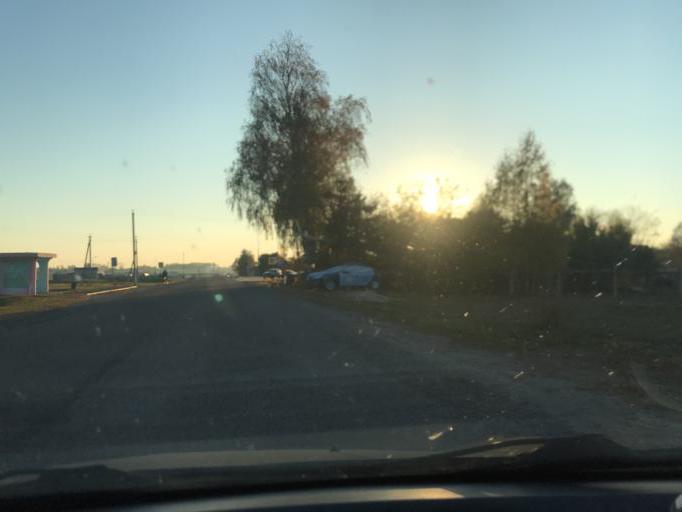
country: BY
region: Gomel
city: Brahin
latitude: 51.8099
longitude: 30.2838
